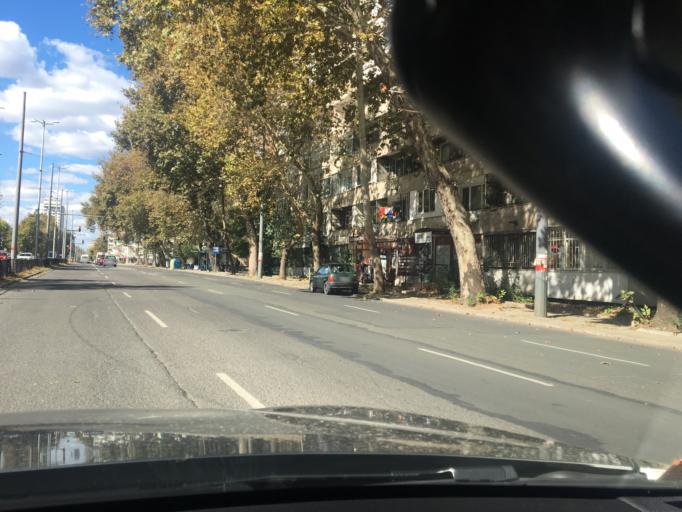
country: BG
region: Burgas
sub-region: Obshtina Burgas
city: Burgas
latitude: 42.5060
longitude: 27.4724
